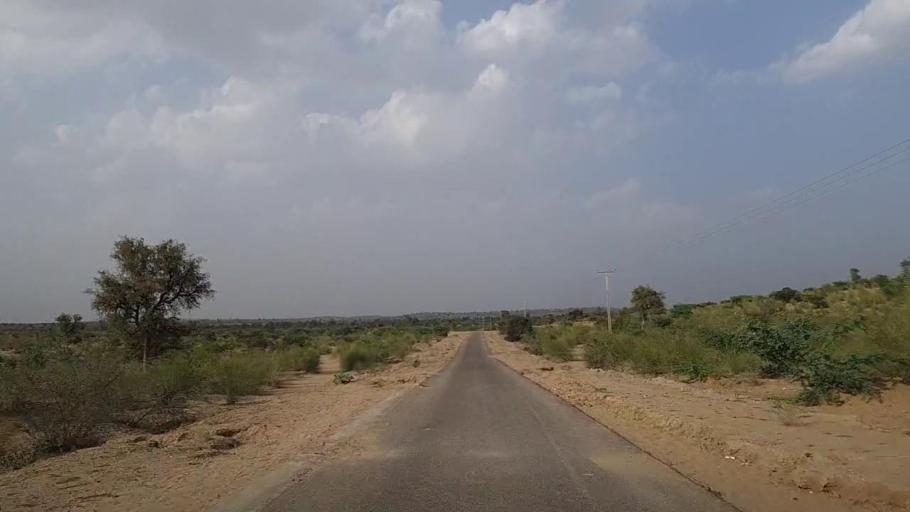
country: PK
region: Sindh
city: Islamkot
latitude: 24.7912
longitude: 70.2014
